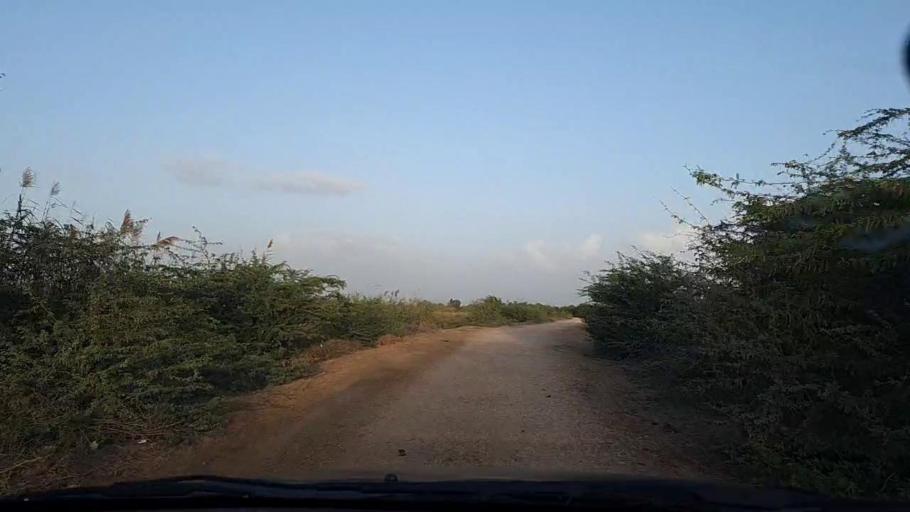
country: PK
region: Sindh
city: Keti Bandar
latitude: 24.1612
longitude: 67.5901
